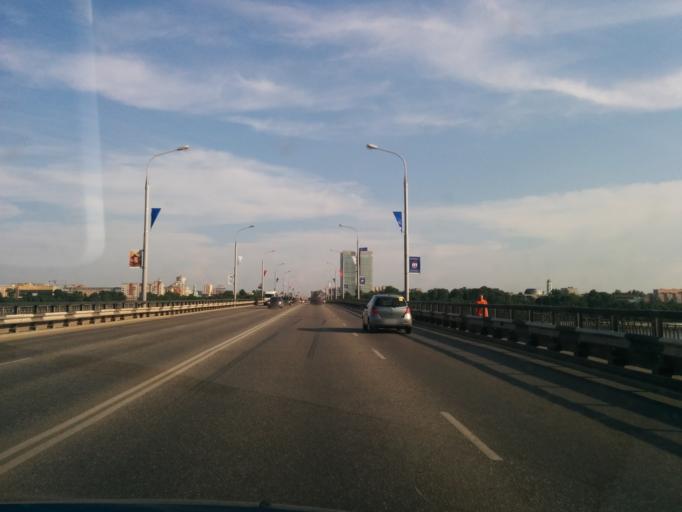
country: RU
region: Perm
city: Perm
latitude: 58.0233
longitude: 56.2197
